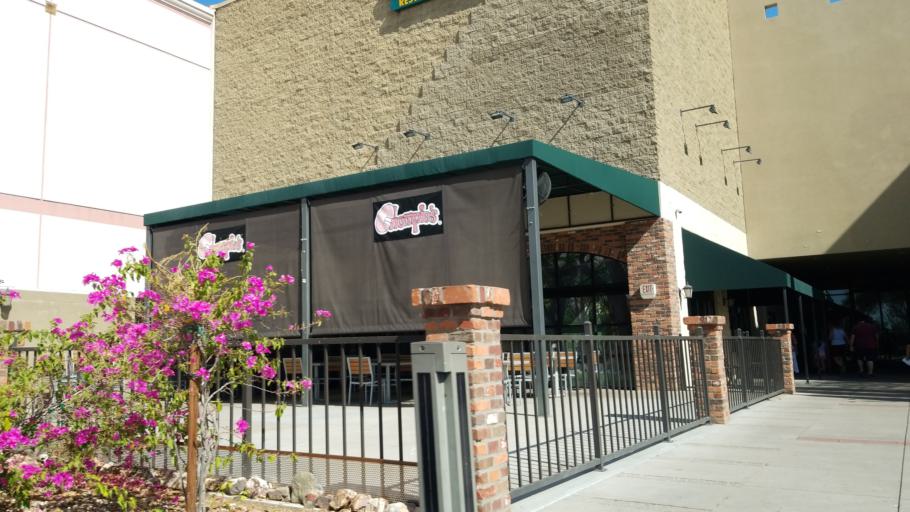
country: US
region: Arizona
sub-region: Maricopa County
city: Peoria
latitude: 33.6415
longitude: -112.2236
